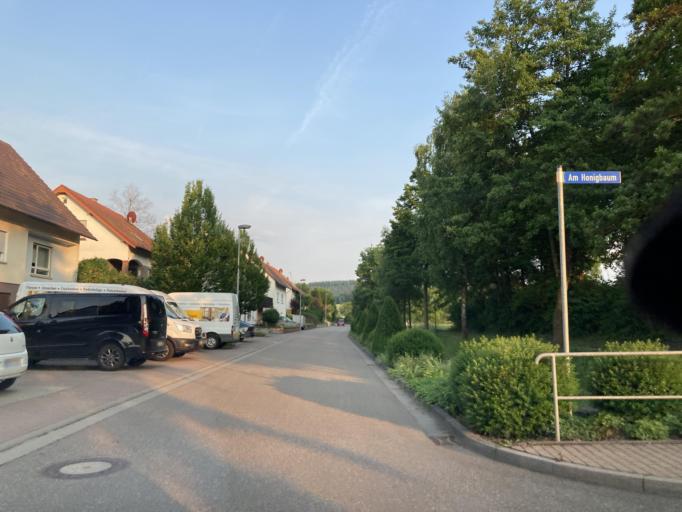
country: DE
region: Baden-Wuerttemberg
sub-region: Karlsruhe Region
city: Sulzfeld
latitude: 49.1006
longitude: 8.8607
